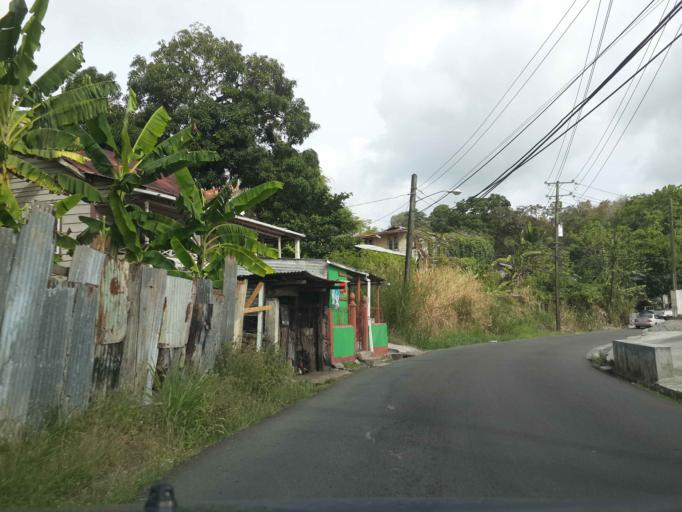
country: LC
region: Castries Quarter
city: Bisee
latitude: 14.0191
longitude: -60.9852
